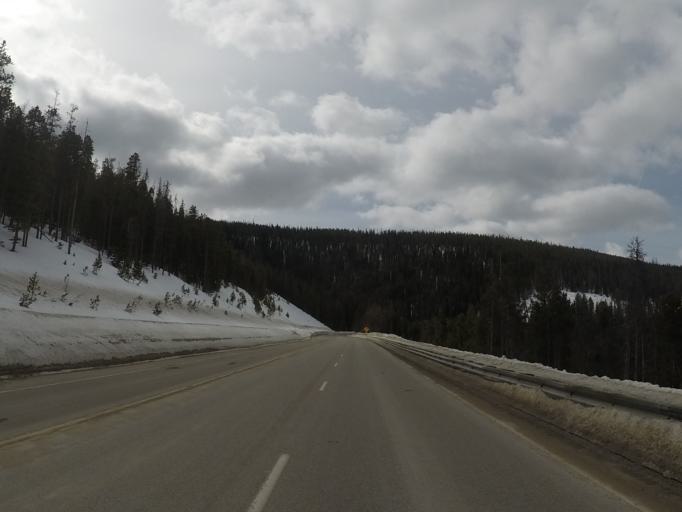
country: US
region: Idaho
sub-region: Lemhi County
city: Salmon
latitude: 45.7086
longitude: -113.9345
